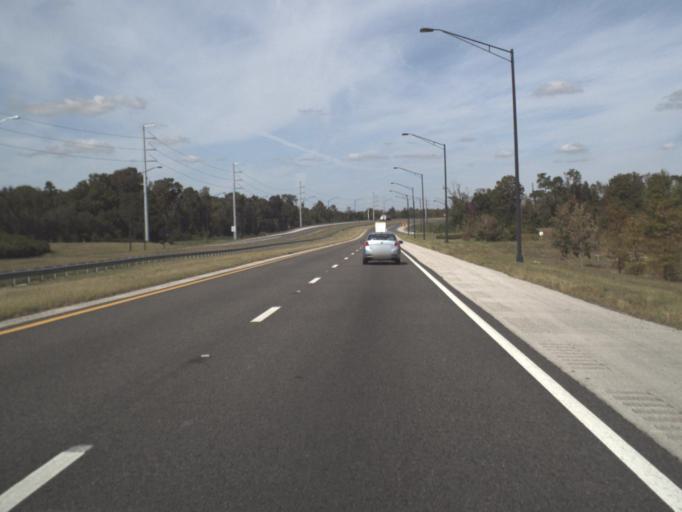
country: US
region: Florida
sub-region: Polk County
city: Citrus Ridge
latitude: 28.2968
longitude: -81.6037
